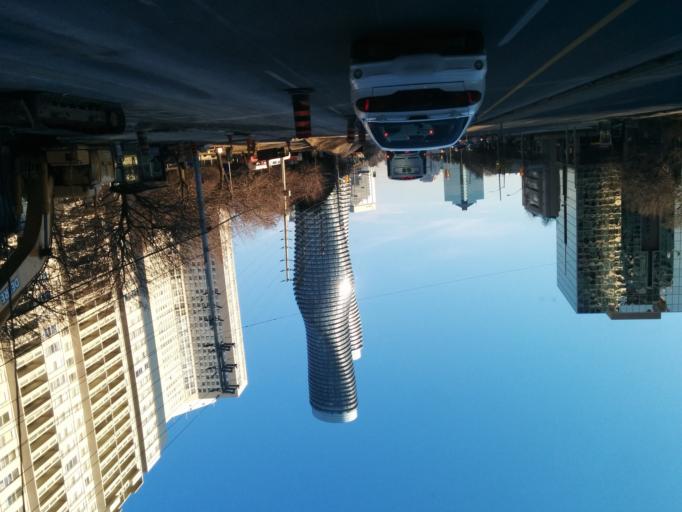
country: CA
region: Ontario
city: Mississauga
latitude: 43.5916
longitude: -79.6323
